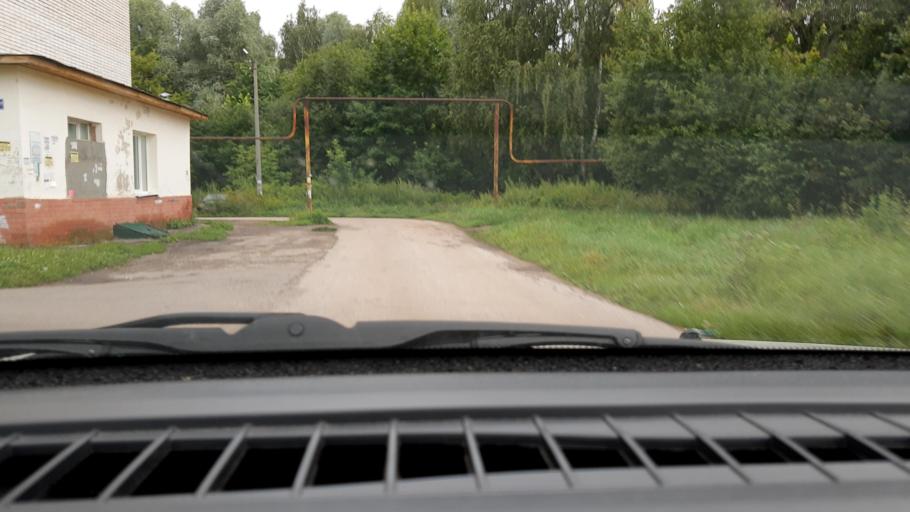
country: RU
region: Nizjnij Novgorod
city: Bogorodsk
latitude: 56.0980
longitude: 43.4771
